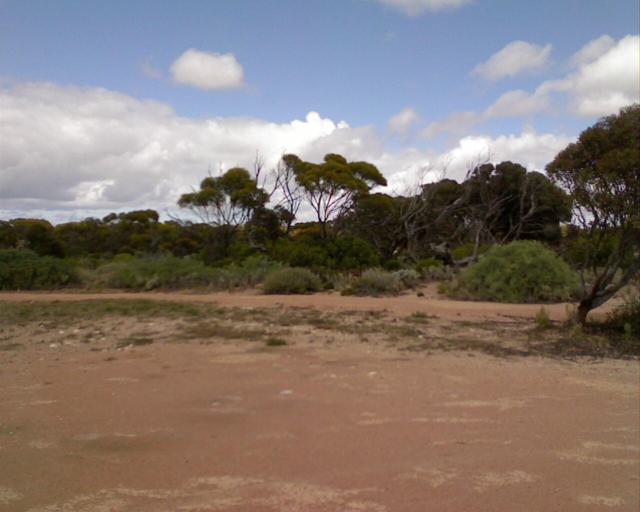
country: AU
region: South Australia
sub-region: Ceduna
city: Ceduna
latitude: -32.1012
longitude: 133.5756
